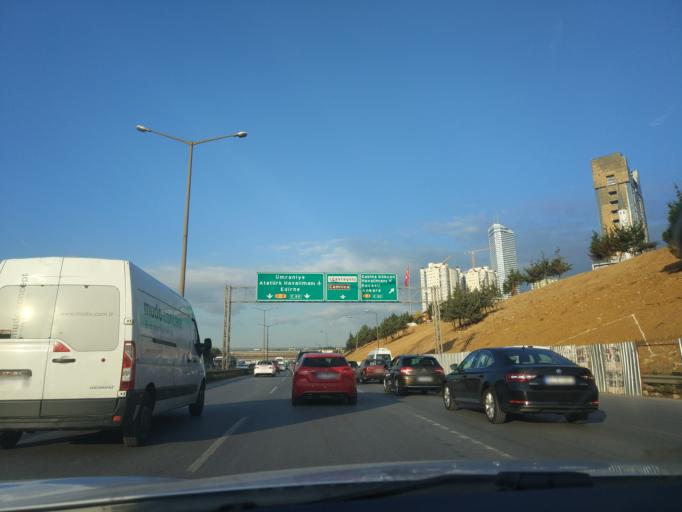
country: TR
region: Istanbul
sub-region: Atasehir
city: Atasehir
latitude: 40.9896
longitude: 29.1105
